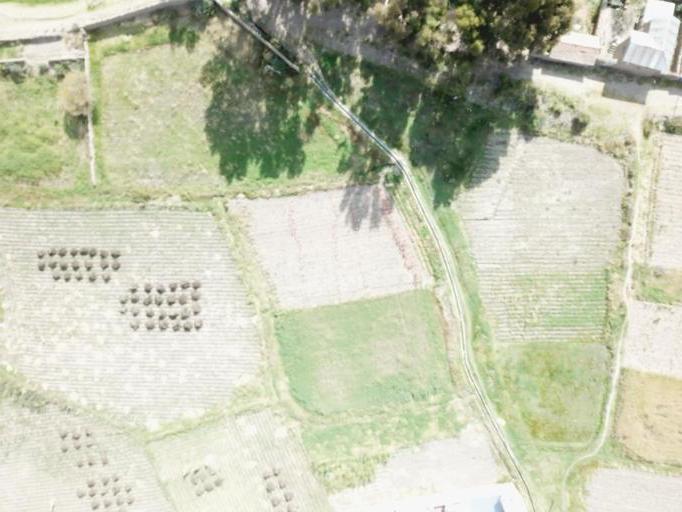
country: BO
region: La Paz
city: Achacachi
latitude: -16.0540
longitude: -68.8159
